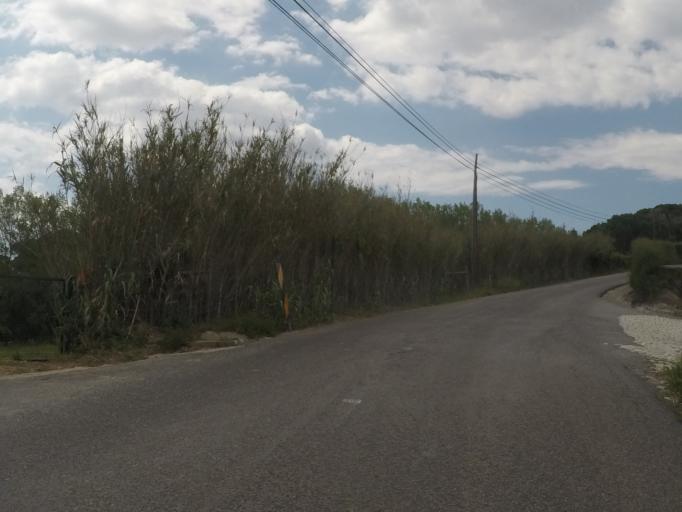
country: PT
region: Setubal
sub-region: Palmela
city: Quinta do Anjo
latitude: 38.5069
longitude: -9.0008
